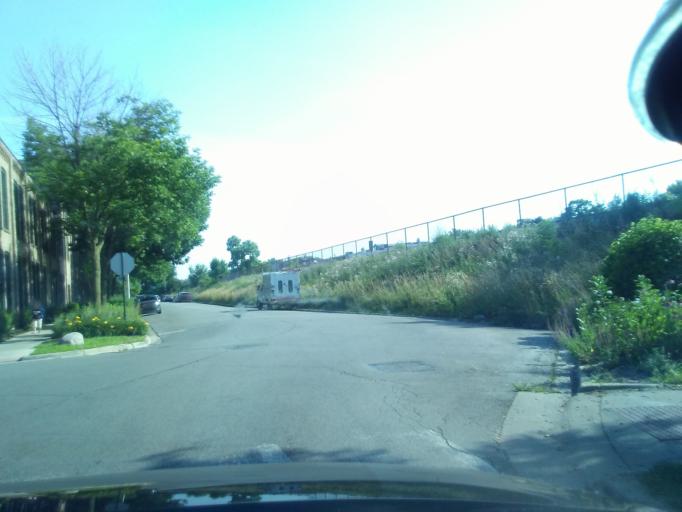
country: US
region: Illinois
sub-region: Cook County
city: Lincolnwood
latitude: 41.9780
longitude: -87.6744
